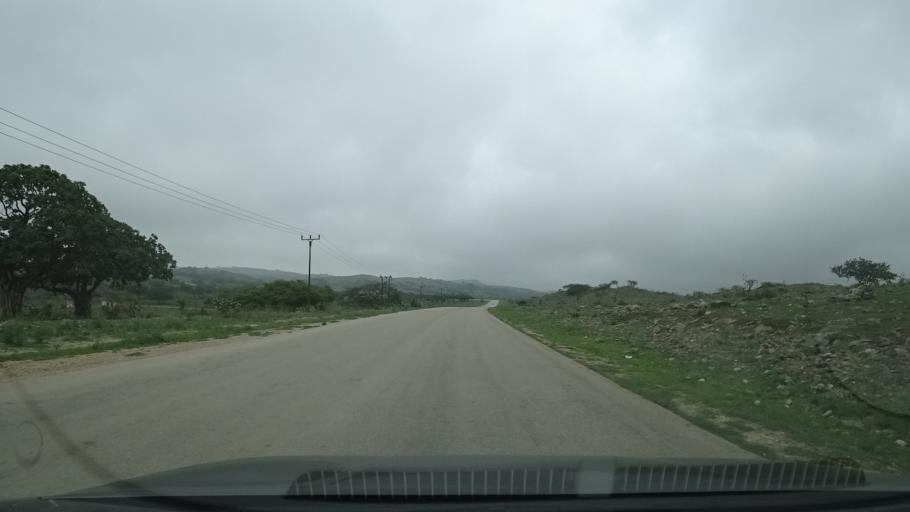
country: OM
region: Zufar
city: Salalah
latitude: 17.1192
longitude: 54.5685
